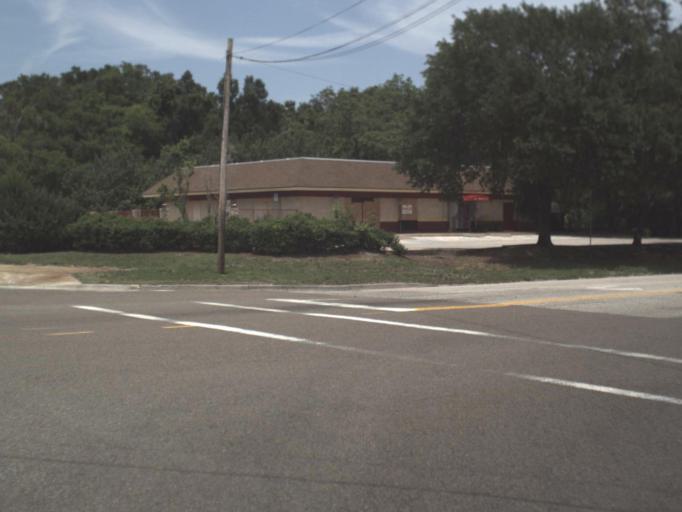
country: US
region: Florida
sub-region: Duval County
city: Jacksonville
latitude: 30.3763
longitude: -81.6511
